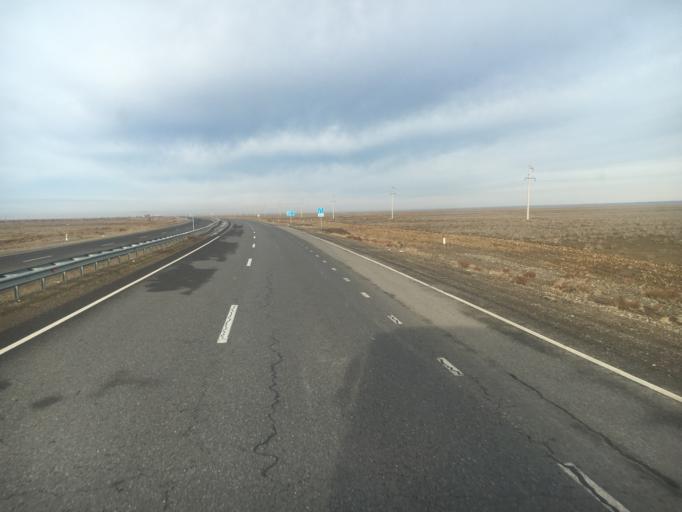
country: KZ
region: Ongtustik Qazaqstan
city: Turkestan
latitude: 43.5006
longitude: 67.8453
